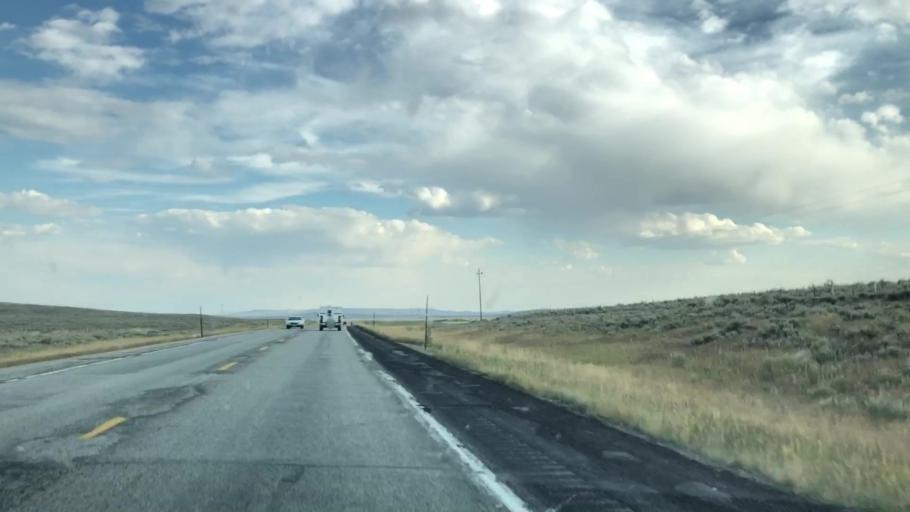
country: US
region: Wyoming
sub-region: Sublette County
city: Pinedale
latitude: 43.0559
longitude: -110.1556
